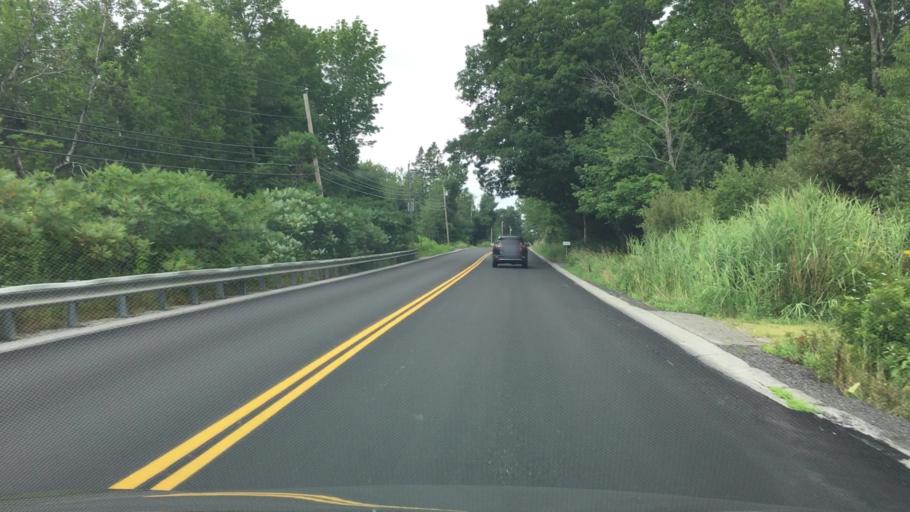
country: US
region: Maine
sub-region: Waldo County
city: Winterport
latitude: 44.6231
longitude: -68.8325
